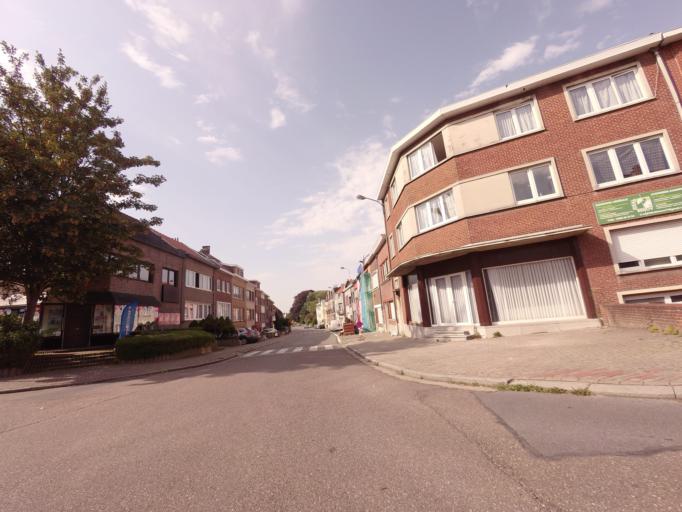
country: BE
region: Flanders
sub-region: Provincie Vlaams-Brabant
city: Grimbergen
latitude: 50.9048
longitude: 4.3606
